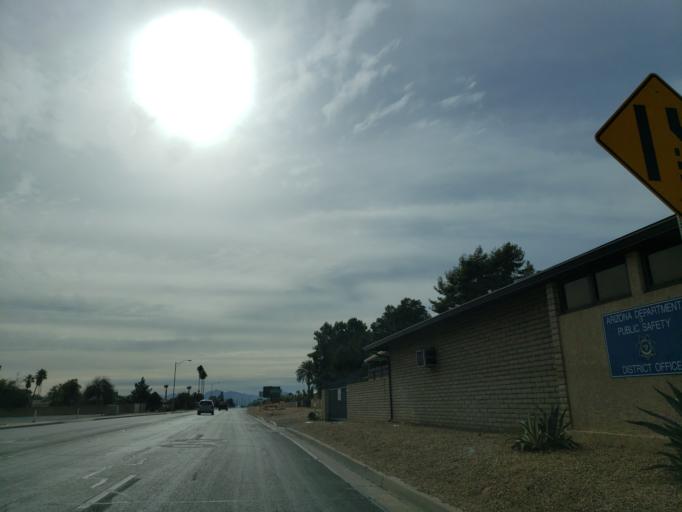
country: US
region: Arizona
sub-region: Maricopa County
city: Youngtown
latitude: 33.5798
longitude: -112.2988
